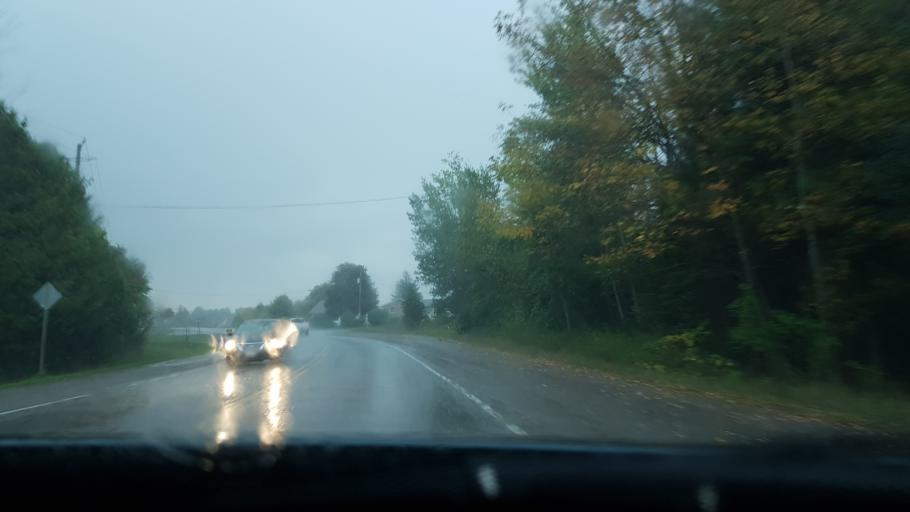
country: CA
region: Ontario
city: Omemee
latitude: 44.3420
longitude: -78.5454
